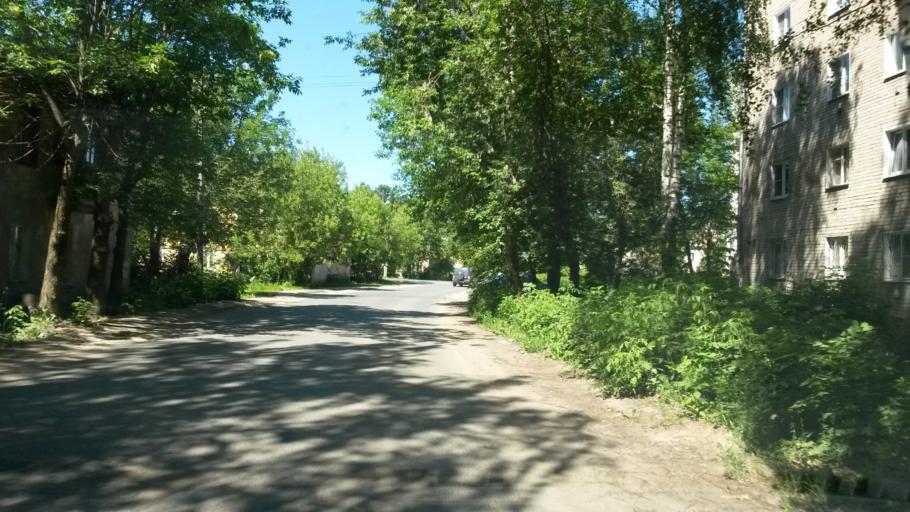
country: RU
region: Ivanovo
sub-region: Gorod Ivanovo
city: Ivanovo
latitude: 56.9819
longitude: 40.9591
